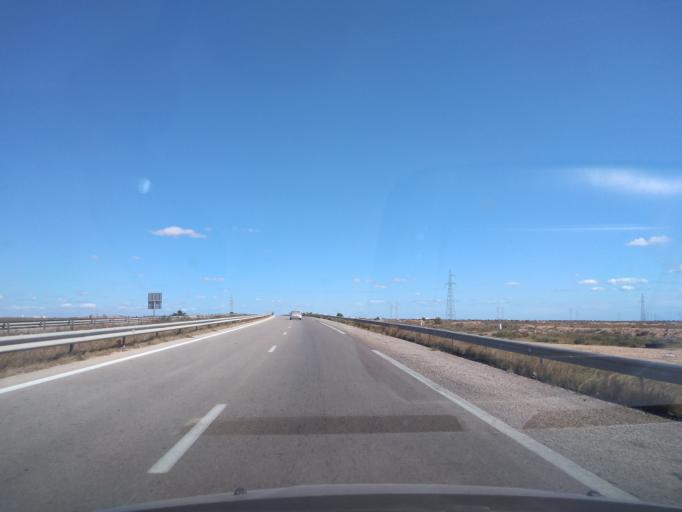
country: TN
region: Safaqis
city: Al Qarmadah
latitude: 34.9037
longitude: 10.7309
